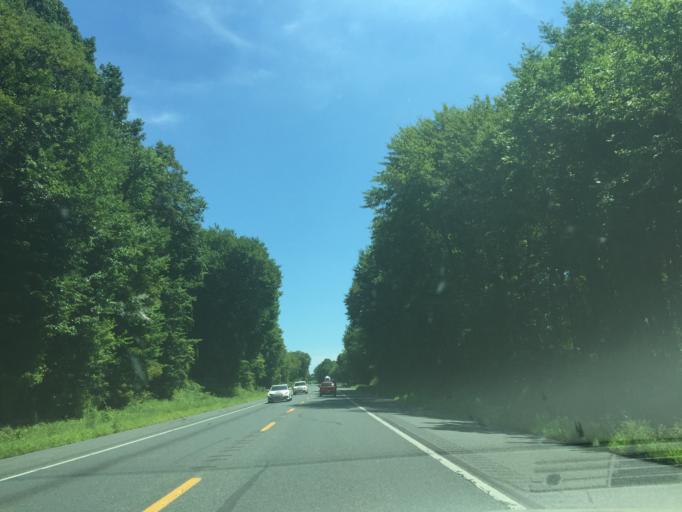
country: US
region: Maryland
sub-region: Harford County
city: Bel Air North
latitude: 39.5723
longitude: -76.3653
